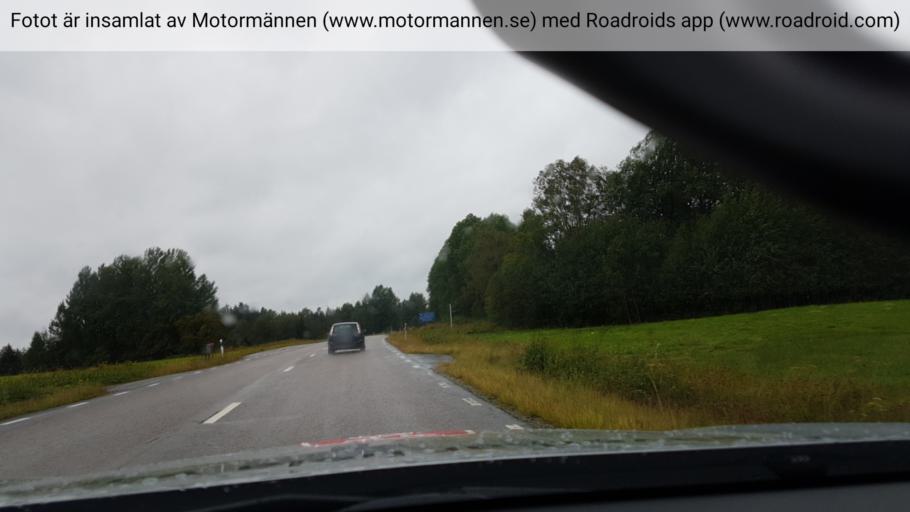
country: SE
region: Vaestra Goetaland
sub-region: Dals-Ed Kommun
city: Ed
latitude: 58.8818
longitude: 11.9034
